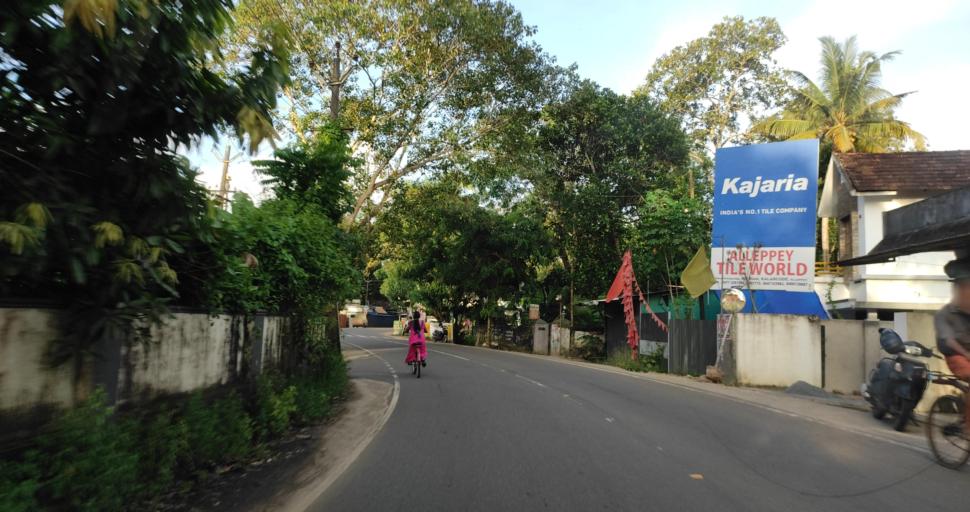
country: IN
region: Kerala
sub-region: Alappuzha
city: Shertallai
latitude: 9.6082
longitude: 76.3361
